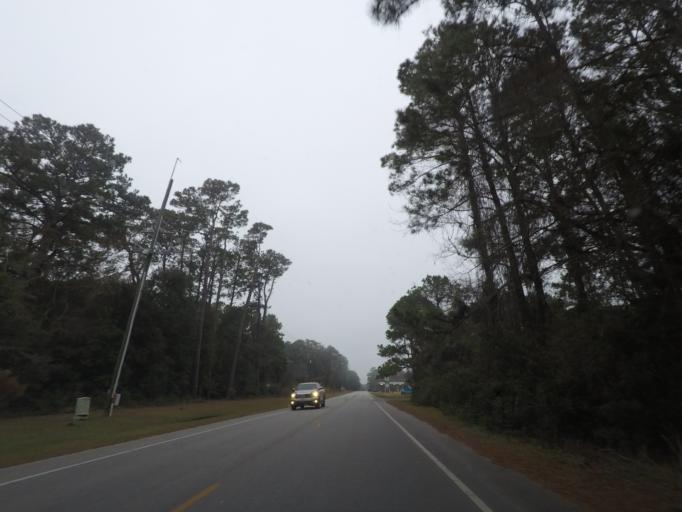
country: US
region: South Carolina
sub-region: Charleston County
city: Seabrook Island
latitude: 32.5142
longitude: -80.2997
